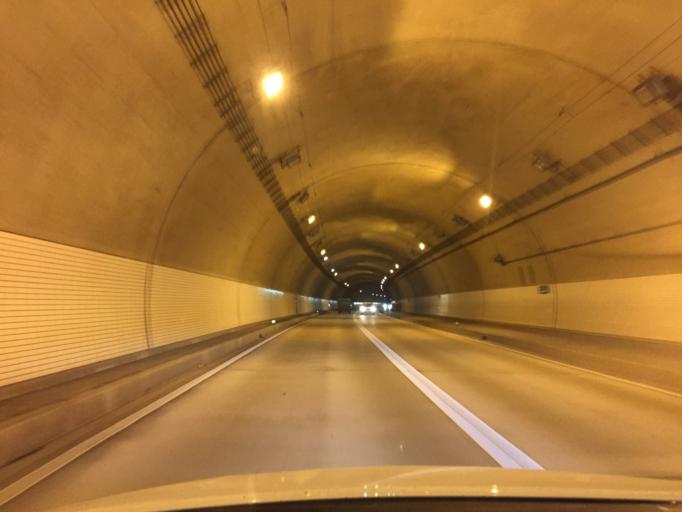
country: JP
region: Fukushima
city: Iwaki
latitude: 37.1260
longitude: 140.7269
